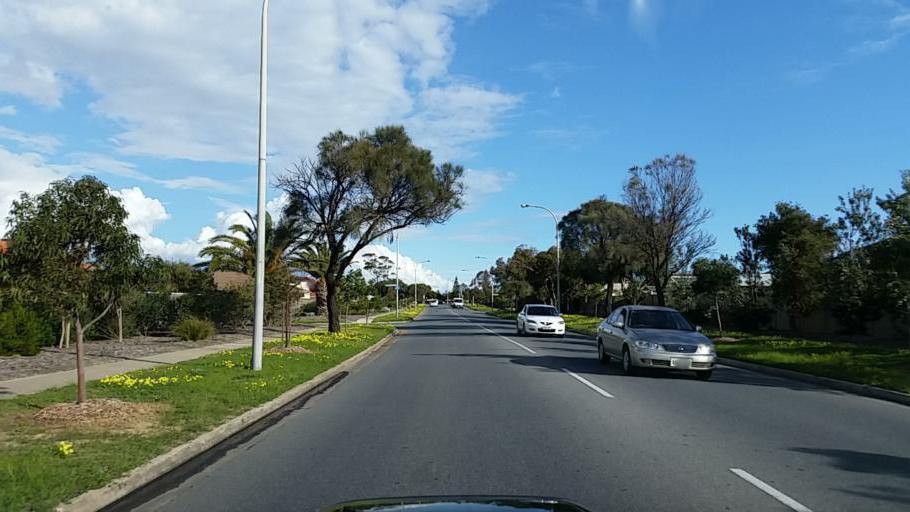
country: AU
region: South Australia
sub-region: Charles Sturt
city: West Lakes Shore
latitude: -34.8687
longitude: 138.4836
